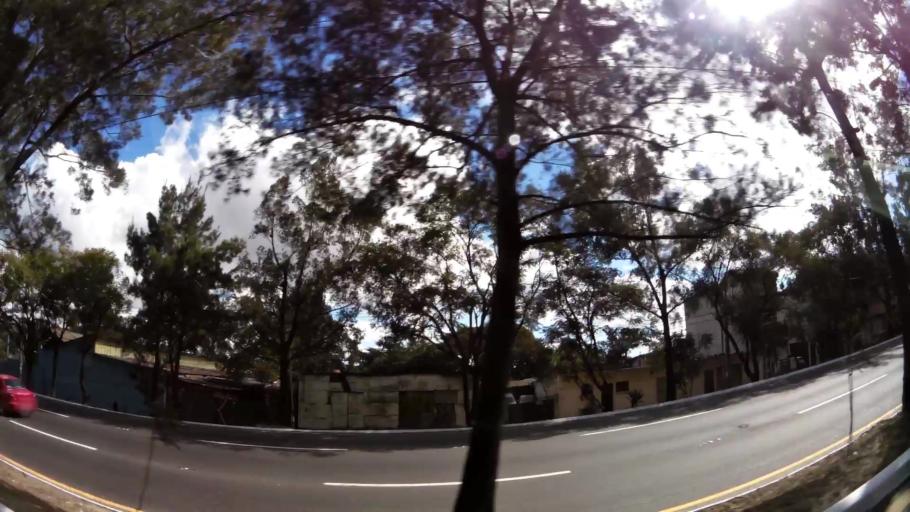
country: GT
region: Guatemala
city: Guatemala City
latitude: 14.6429
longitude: -90.5439
